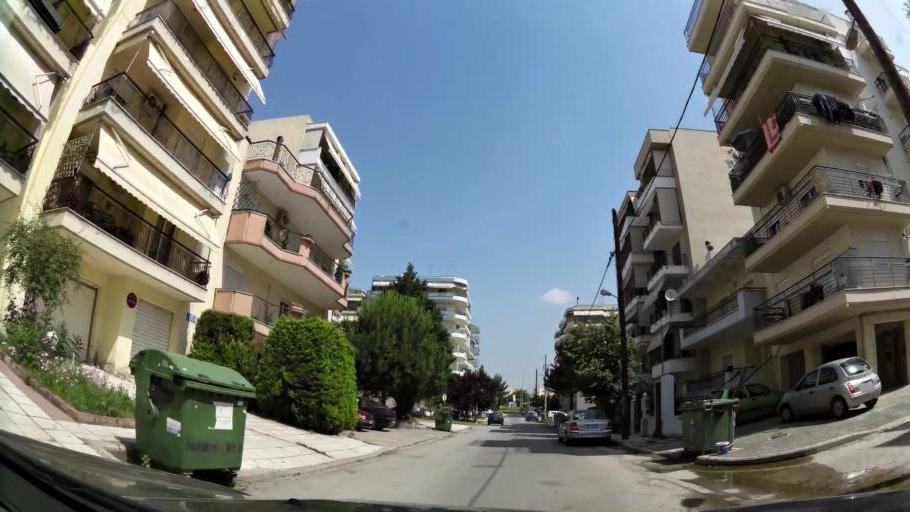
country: GR
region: Central Macedonia
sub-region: Nomos Thessalonikis
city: Evosmos
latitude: 40.6758
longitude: 22.9221
